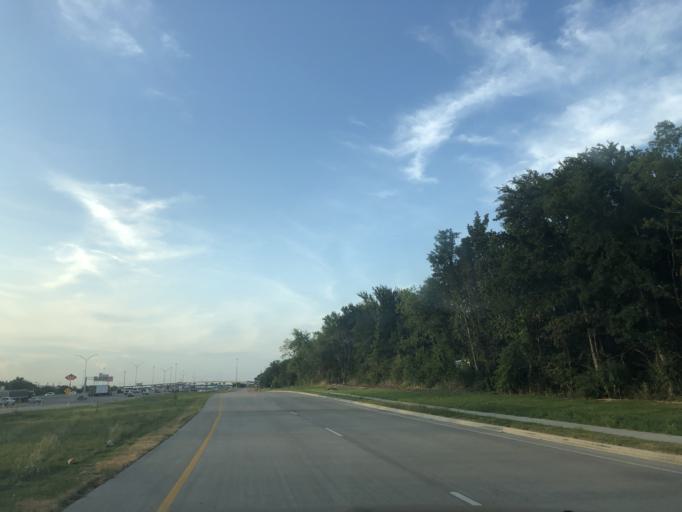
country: US
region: Texas
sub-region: Dallas County
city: Mesquite
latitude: 32.7817
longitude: -96.6236
